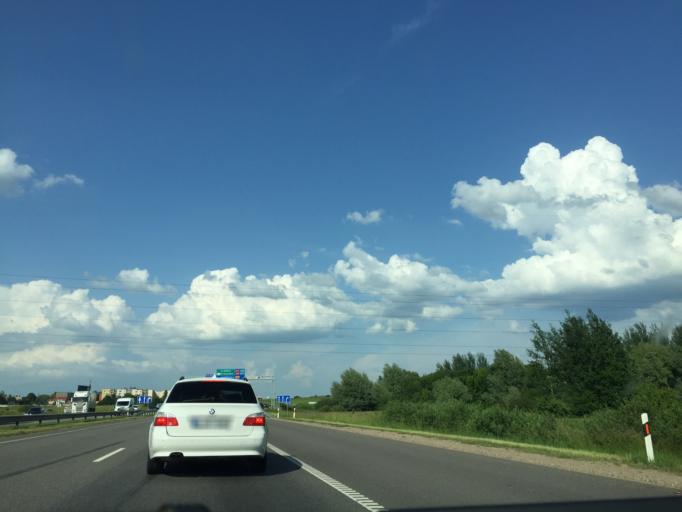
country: LT
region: Kauno apskritis
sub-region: Kaunas
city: Silainiai
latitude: 54.9378
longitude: 23.8768
